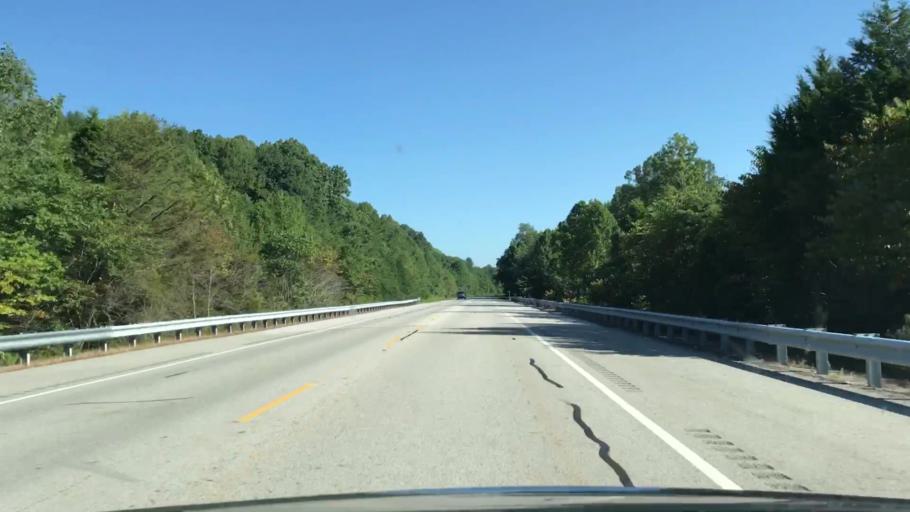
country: US
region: Tennessee
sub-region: Clay County
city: Celina
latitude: 36.5876
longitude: -85.4422
